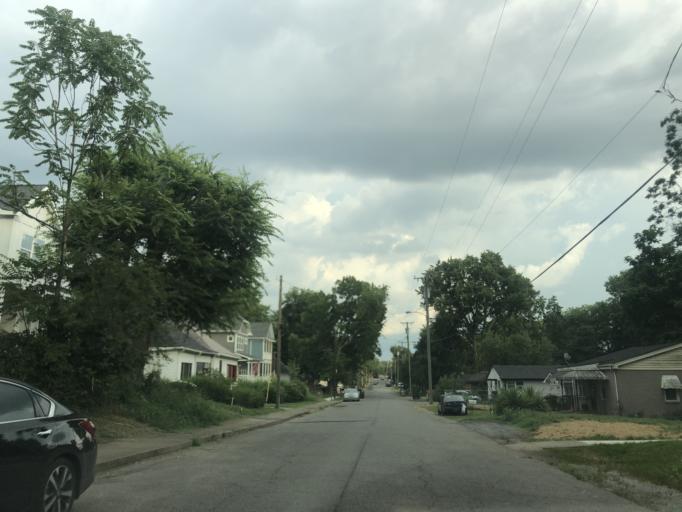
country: US
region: Tennessee
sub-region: Davidson County
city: Nashville
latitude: 36.1782
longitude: -86.8046
